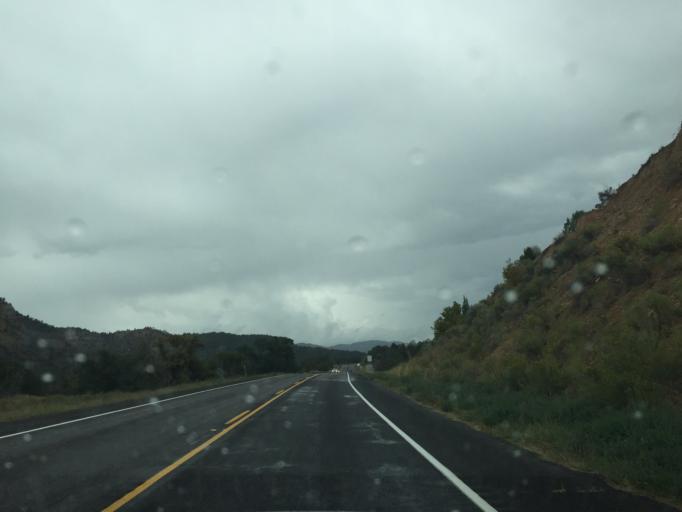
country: US
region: Utah
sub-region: Kane County
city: Kanab
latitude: 37.2910
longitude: -112.6188
